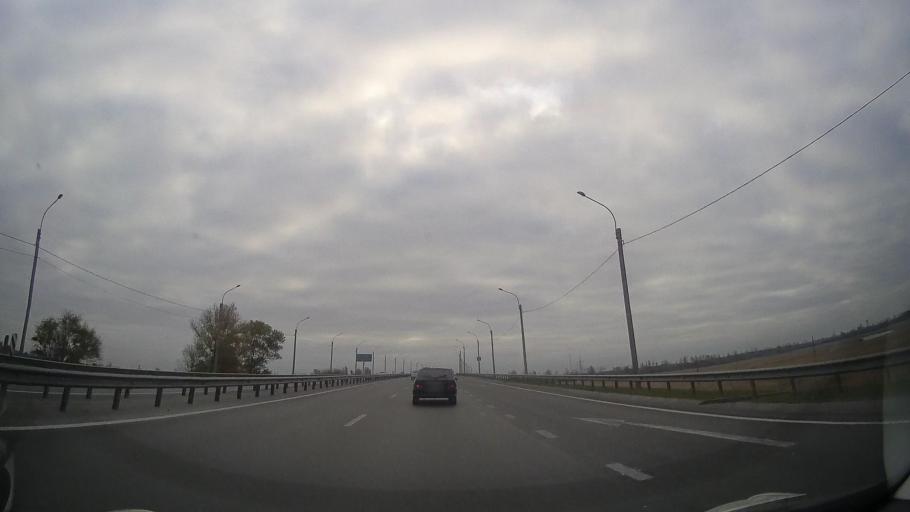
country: RU
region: Rostov
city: Bataysk
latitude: 47.1674
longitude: 39.7519
